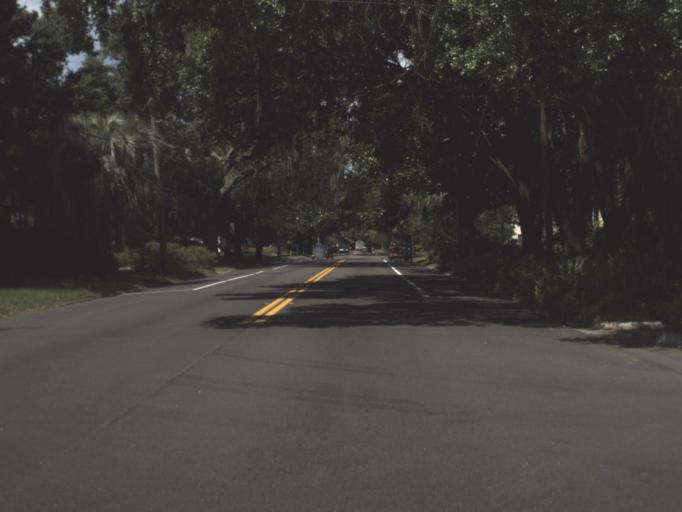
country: US
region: Florida
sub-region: Duval County
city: Jacksonville
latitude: 30.3005
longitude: -81.6993
